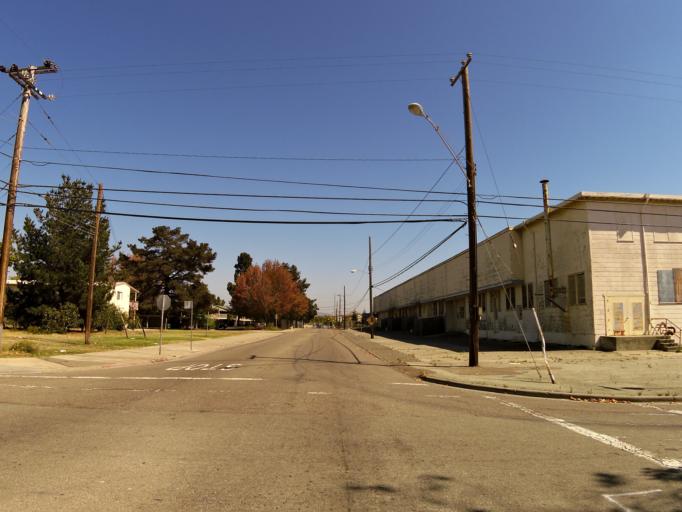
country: US
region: California
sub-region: Alameda County
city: Oakland
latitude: 37.7850
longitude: -122.2942
